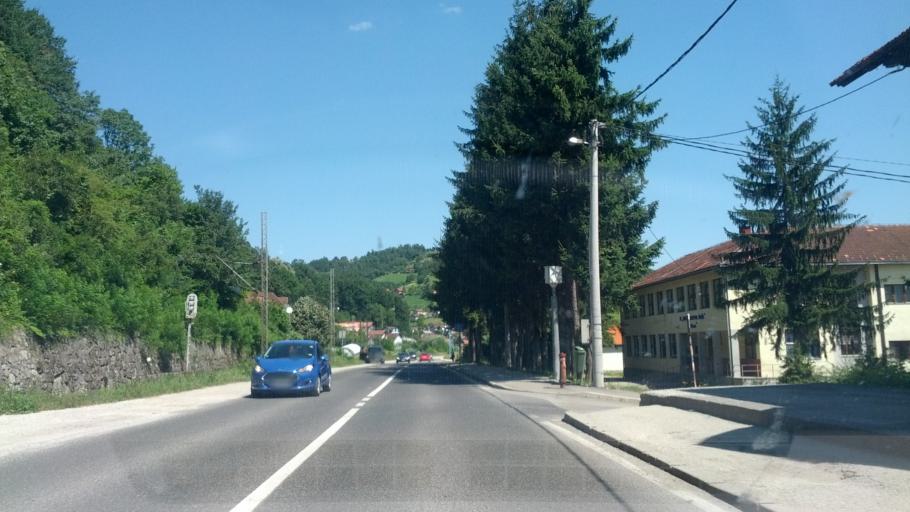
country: BA
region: Federation of Bosnia and Herzegovina
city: Bosanska Krupa
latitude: 44.8894
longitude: 16.1544
